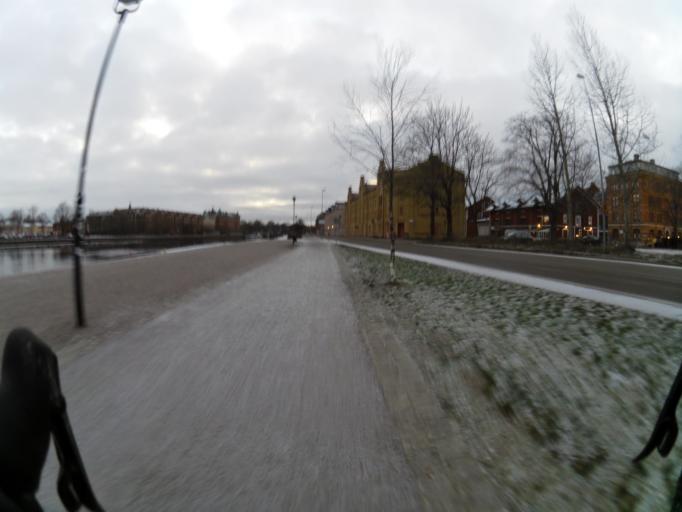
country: SE
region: Gaevleborg
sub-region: Gavle Kommun
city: Gavle
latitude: 60.6779
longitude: 17.1597
